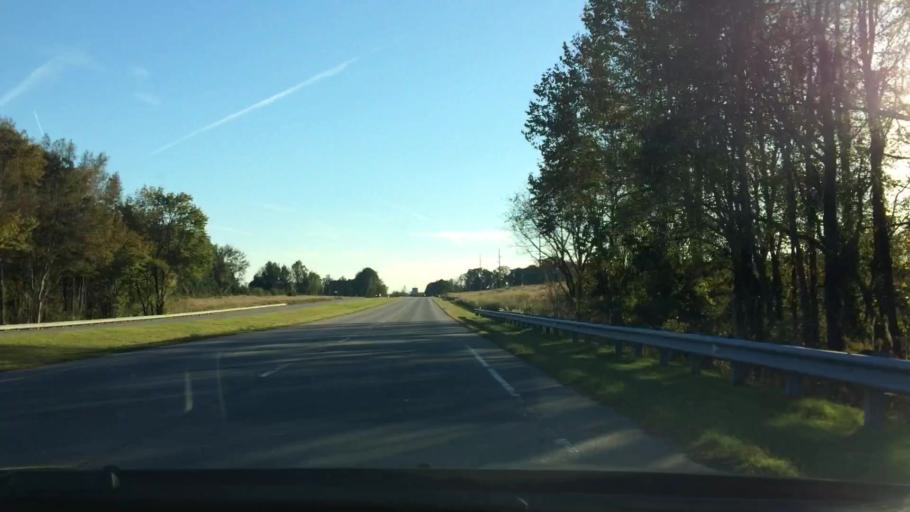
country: US
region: North Carolina
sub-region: Pitt County
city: Grifton
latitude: 35.3998
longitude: -77.4398
